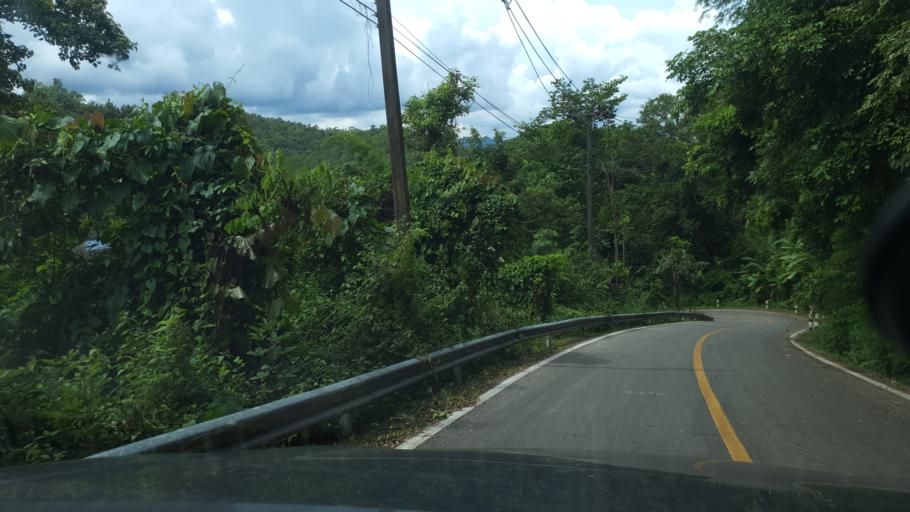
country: TH
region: Lamphun
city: Mae Tha
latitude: 18.5005
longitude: 99.2670
